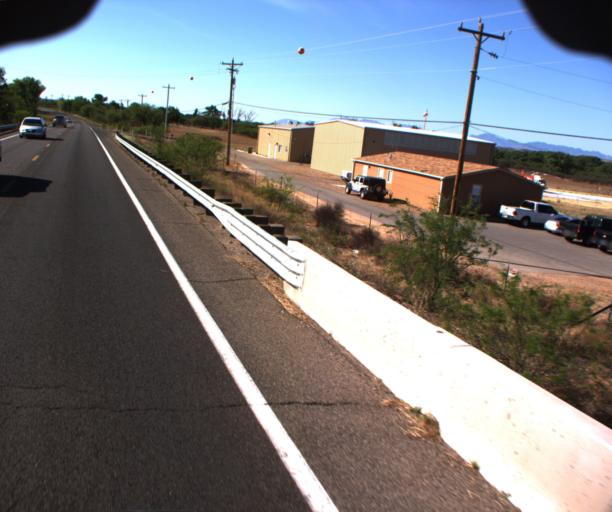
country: US
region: Arizona
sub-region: Cochise County
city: Saint David
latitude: 31.8696
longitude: -110.2082
